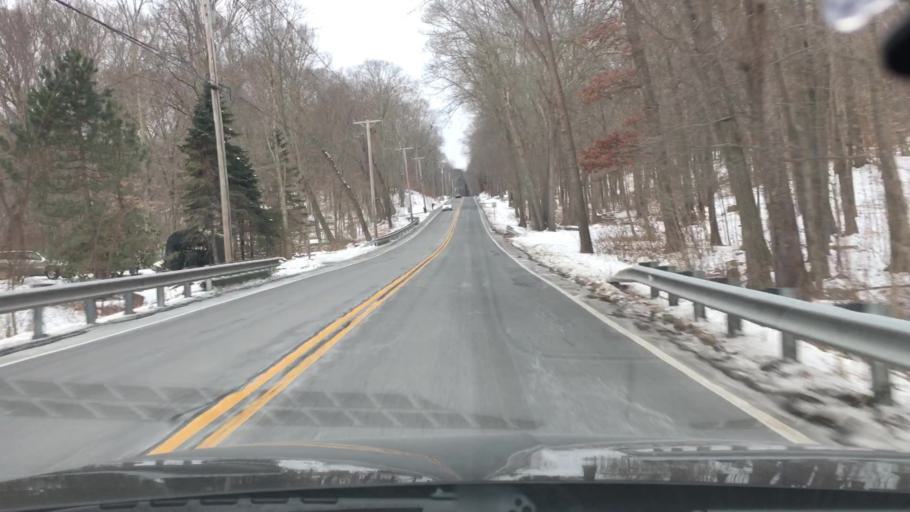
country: US
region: Connecticut
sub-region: Tolland County
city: Tolland
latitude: 41.8431
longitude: -72.3219
